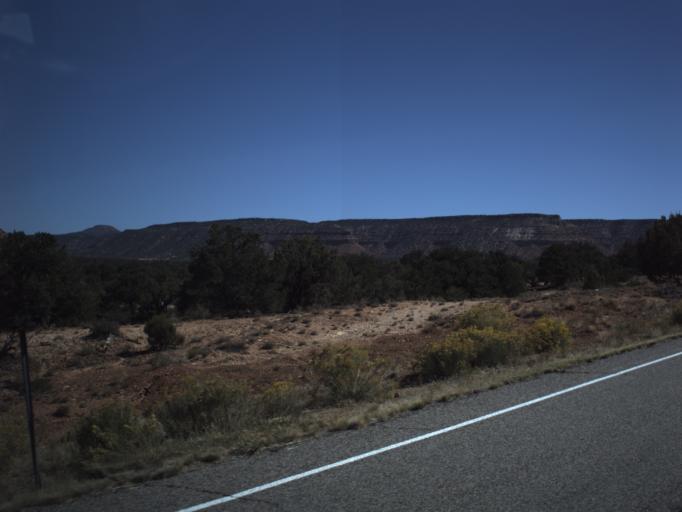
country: US
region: Utah
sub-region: San Juan County
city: Blanding
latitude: 37.6349
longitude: -110.1020
